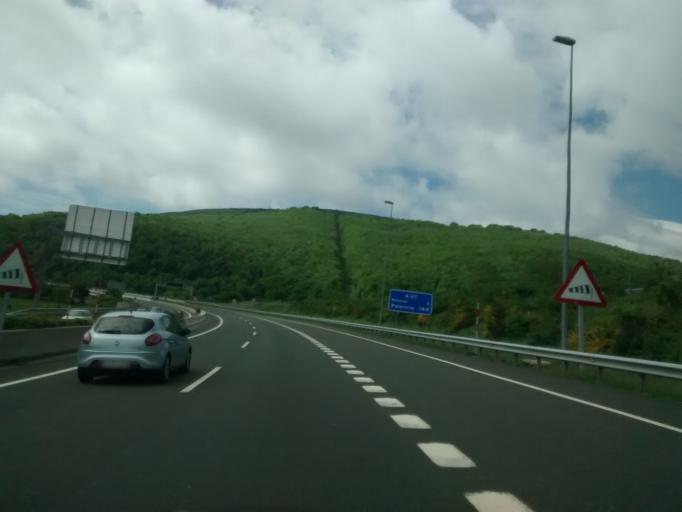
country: ES
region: Cantabria
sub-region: Provincia de Cantabria
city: Santiurde de Reinosa
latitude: 43.0631
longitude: -4.0902
